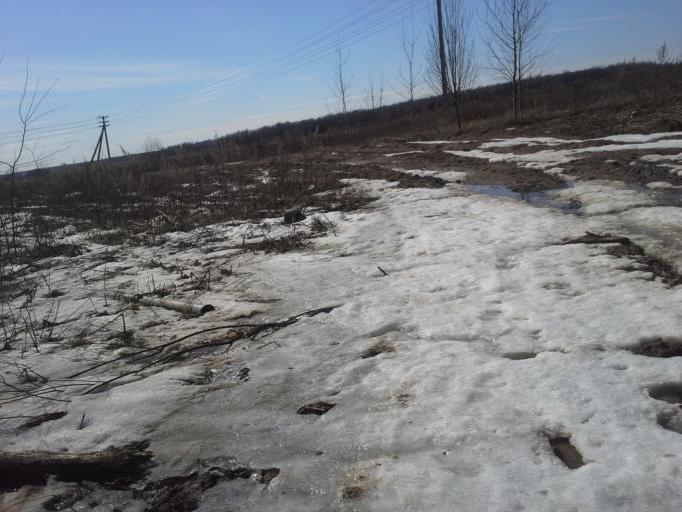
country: RU
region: Moskovskaya
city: Mosrentgen
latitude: 55.5840
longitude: 37.4459
